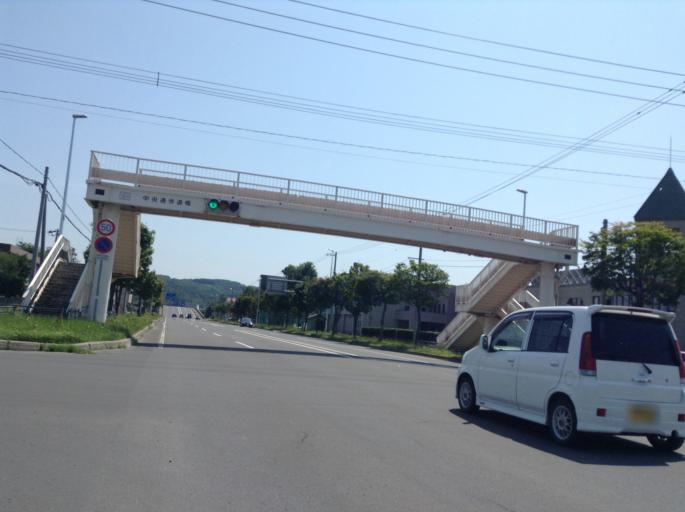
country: JP
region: Hokkaido
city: Nayoro
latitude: 44.3564
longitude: 142.4602
